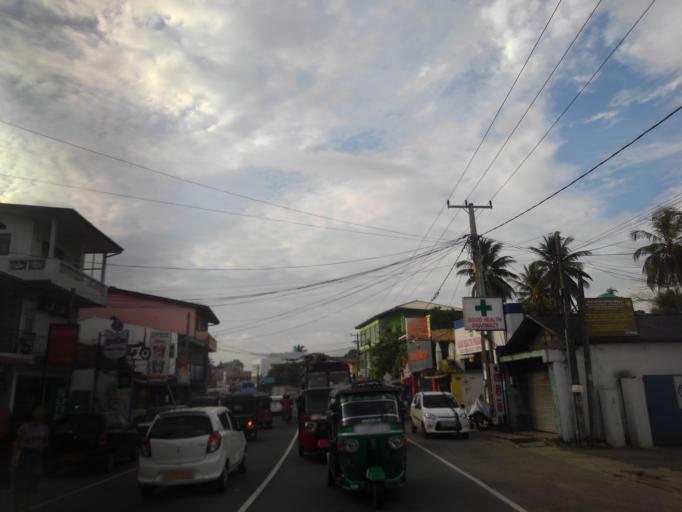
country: LK
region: Southern
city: Unawatuna
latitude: 6.0330
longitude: 80.2390
